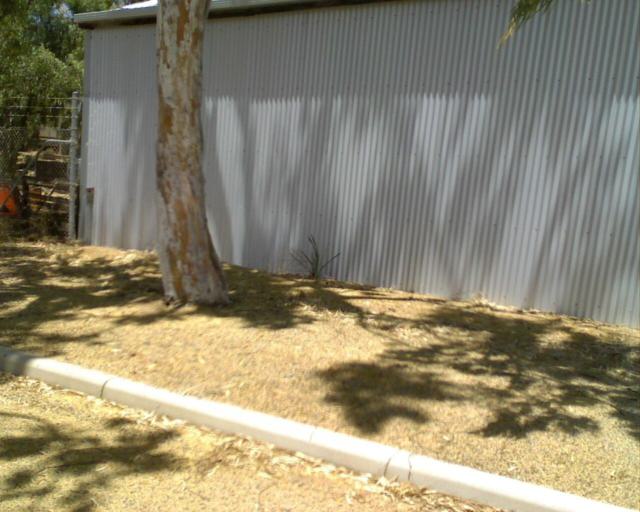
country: AU
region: Western Australia
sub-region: Merredin
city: Merredin
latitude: -30.8108
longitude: 117.8628
